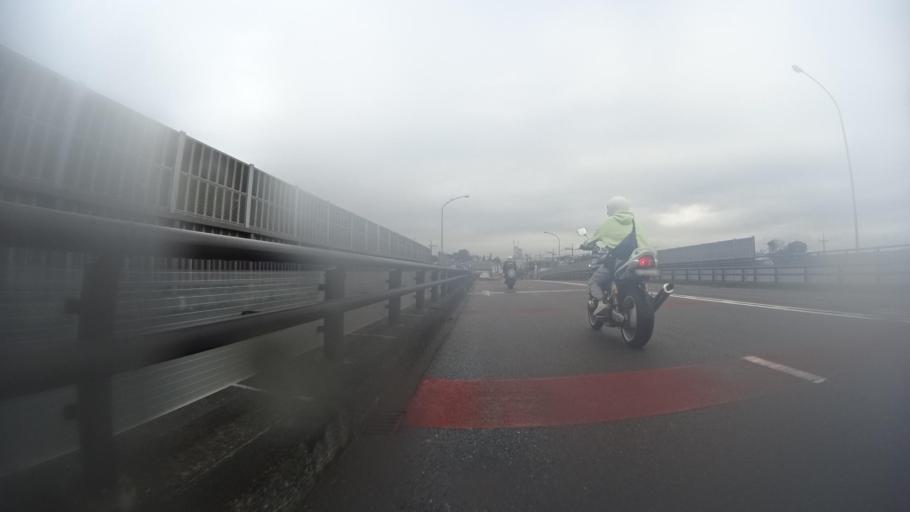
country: JP
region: Tokyo
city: Fussa
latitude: 35.7201
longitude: 139.3269
